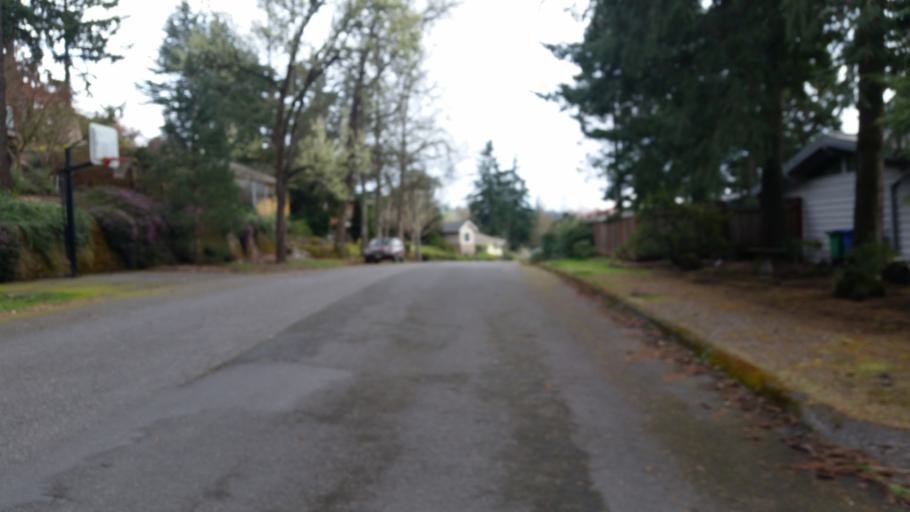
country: US
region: Oregon
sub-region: Washington County
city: Raleigh Hills
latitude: 45.4802
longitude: -122.7196
